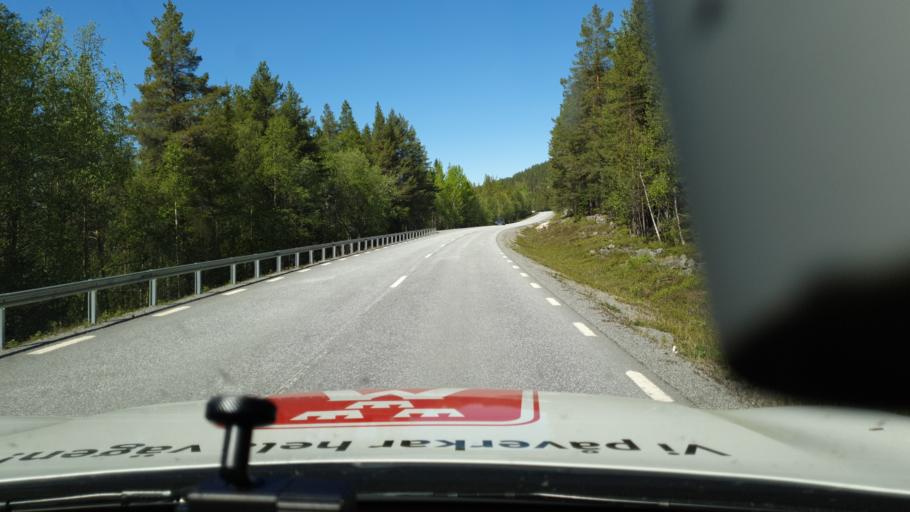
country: SE
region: Vaesterbotten
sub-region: Storumans Kommun
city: Storuman
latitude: 65.1534
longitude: 17.0651
